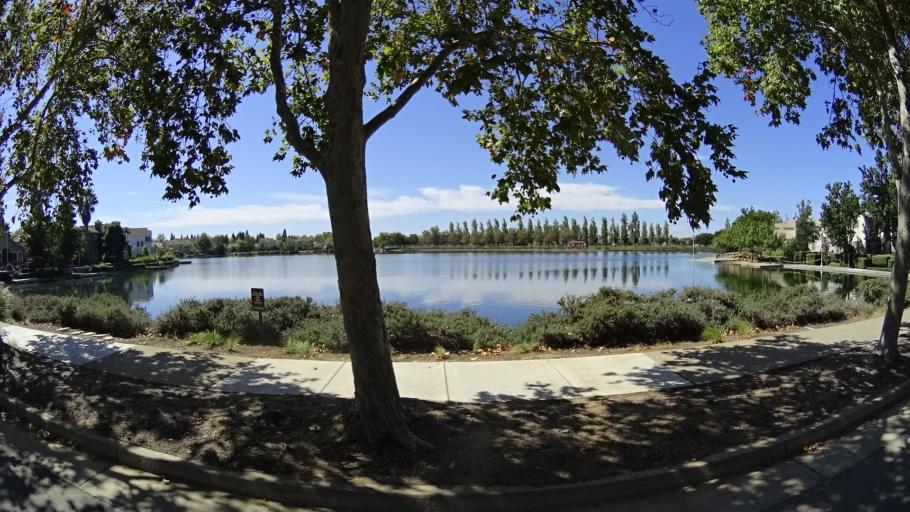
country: US
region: California
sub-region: Sacramento County
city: Laguna
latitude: 38.4229
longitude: -121.4670
